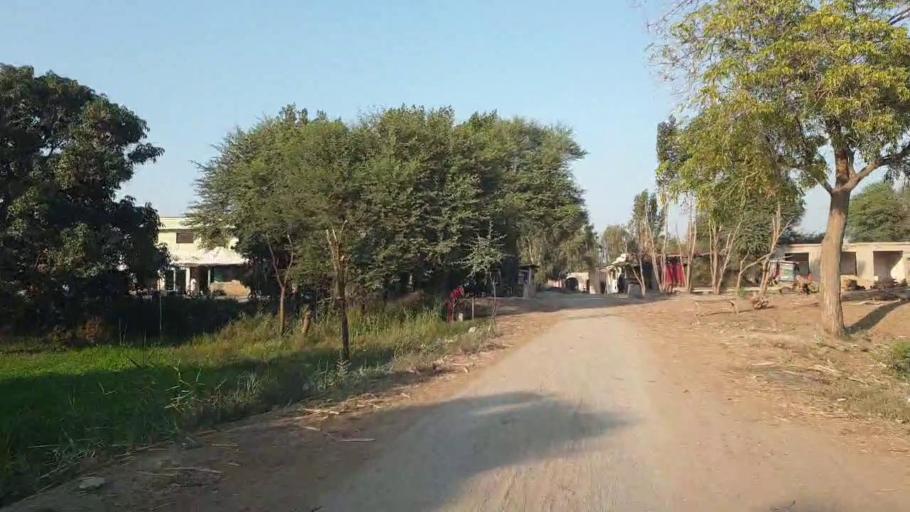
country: PK
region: Sindh
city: Mirpur Khas
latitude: 25.4420
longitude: 68.9134
